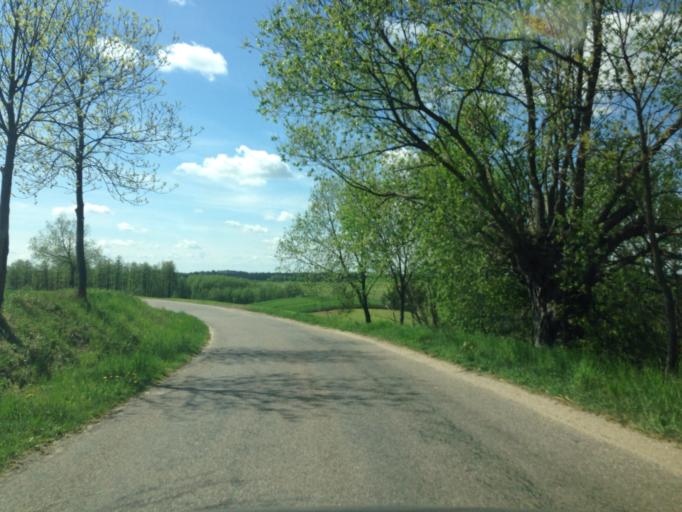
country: PL
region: Kujawsko-Pomorskie
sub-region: Powiat brodnicki
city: Bartniczka
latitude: 53.2803
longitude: 19.6526
